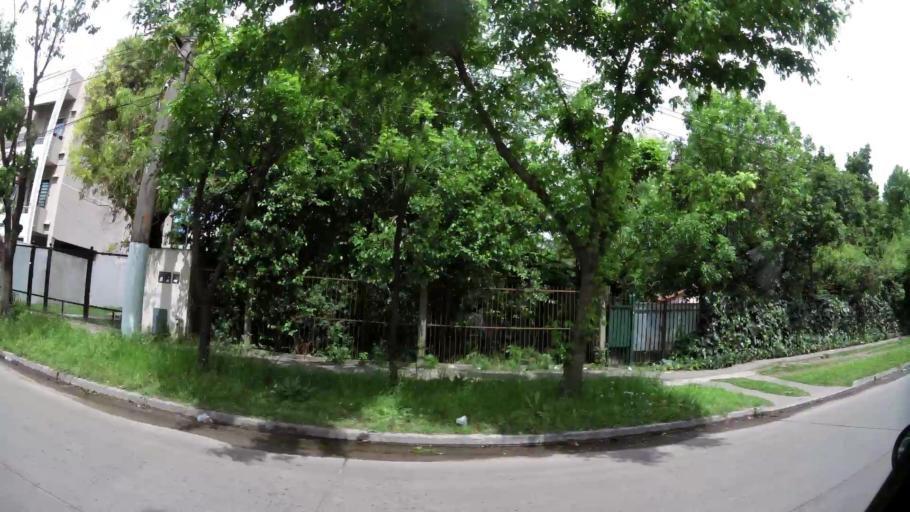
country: AR
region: Buenos Aires
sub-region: Partido de Quilmes
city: Quilmes
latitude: -34.7724
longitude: -58.2652
